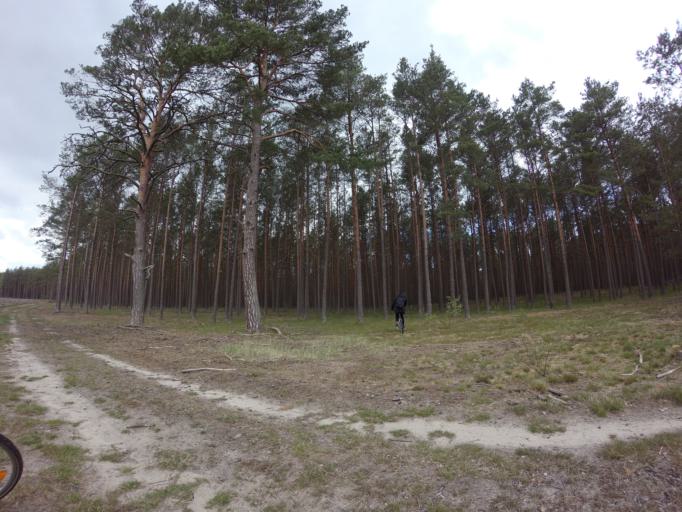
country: PL
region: West Pomeranian Voivodeship
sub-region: Powiat drawski
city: Kalisz Pomorski
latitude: 53.1912
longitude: 15.9982
